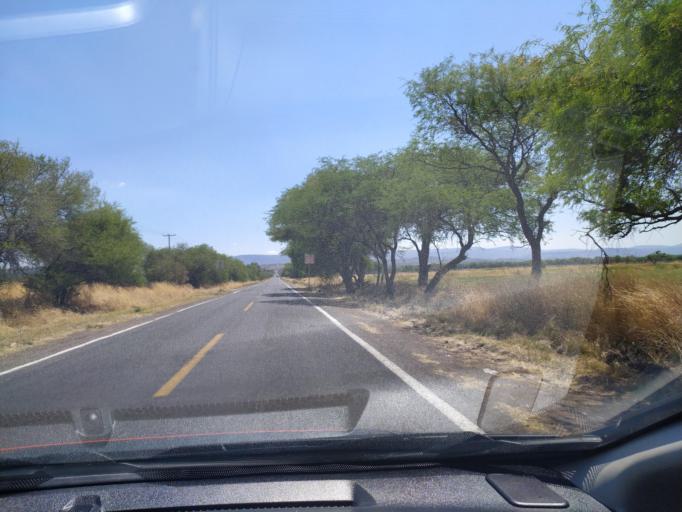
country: MX
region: Guanajuato
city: Ciudad Manuel Doblado
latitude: 20.7601
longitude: -101.8277
